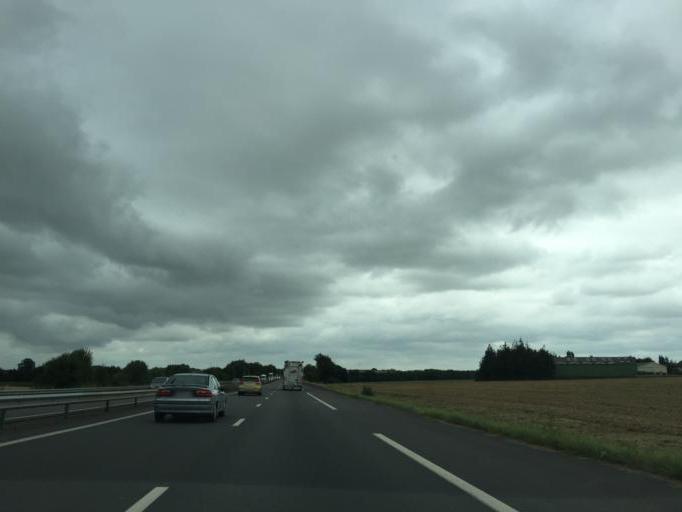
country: FR
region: Brittany
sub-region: Departement d'Ille-et-Vilaine
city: Torce
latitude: 48.0762
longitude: -1.2935
